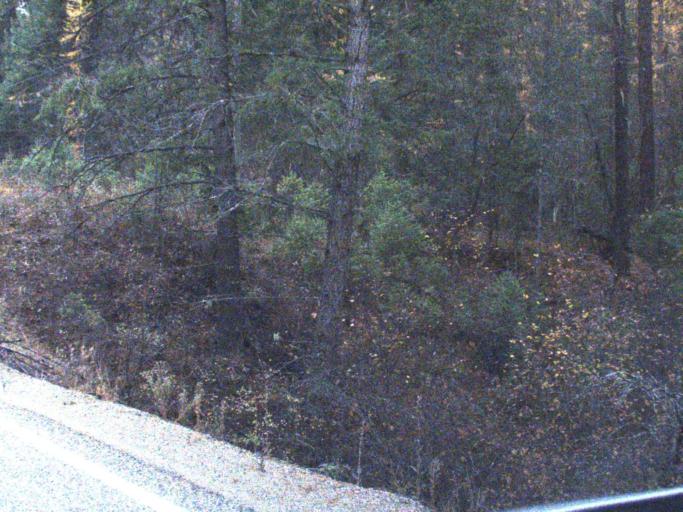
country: CA
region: British Columbia
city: Grand Forks
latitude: 48.9643
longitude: -118.2171
